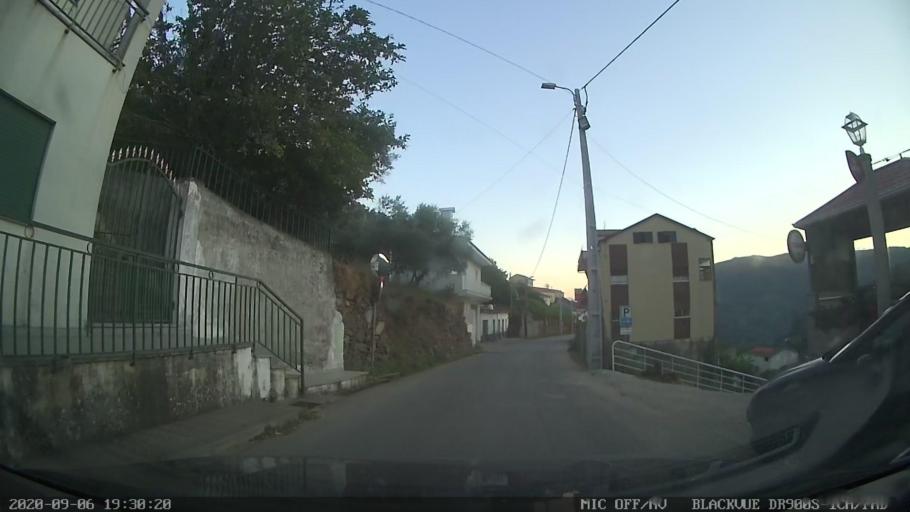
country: PT
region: Vila Real
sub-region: Mesao Frio
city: Mesao Frio
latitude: 41.1856
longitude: -7.9001
